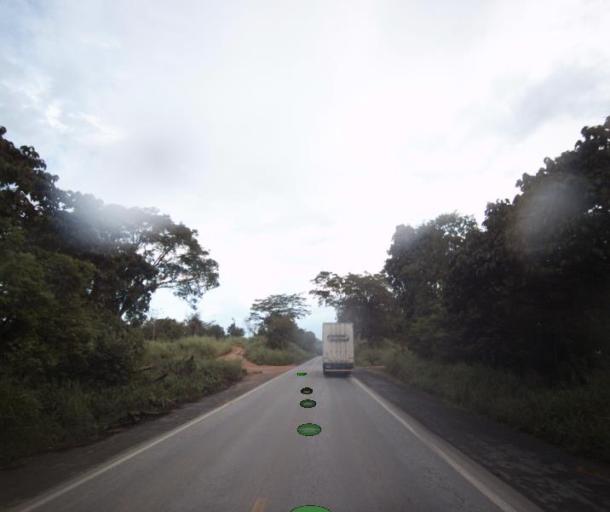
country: BR
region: Goias
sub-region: Porangatu
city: Porangatu
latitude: -13.9467
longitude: -49.0830
